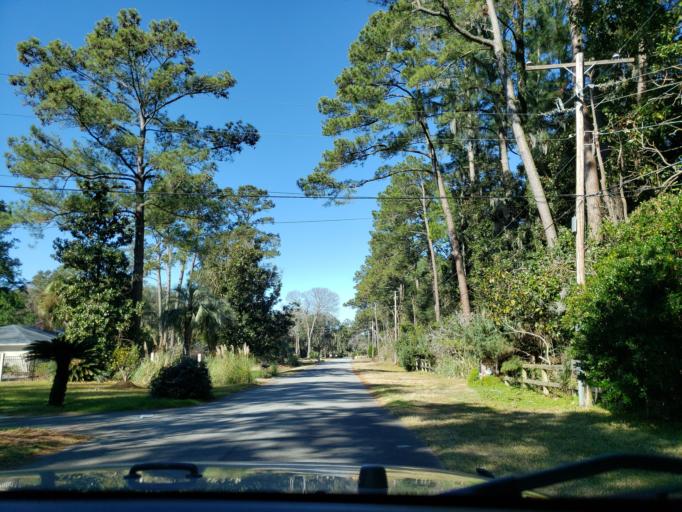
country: US
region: Georgia
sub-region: Chatham County
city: Wilmington Island
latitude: 32.0380
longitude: -80.9667
